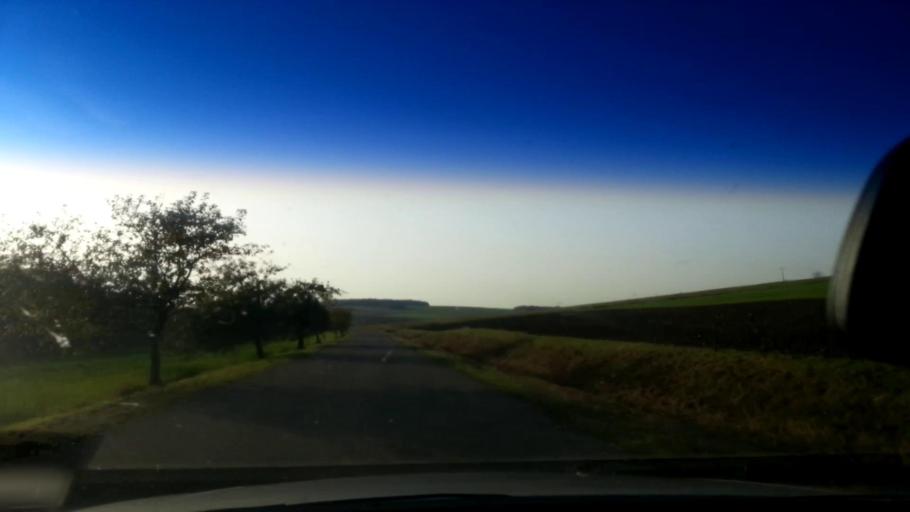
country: DE
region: Bavaria
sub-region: Upper Franconia
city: Ebensfeld
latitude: 50.0273
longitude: 10.9868
